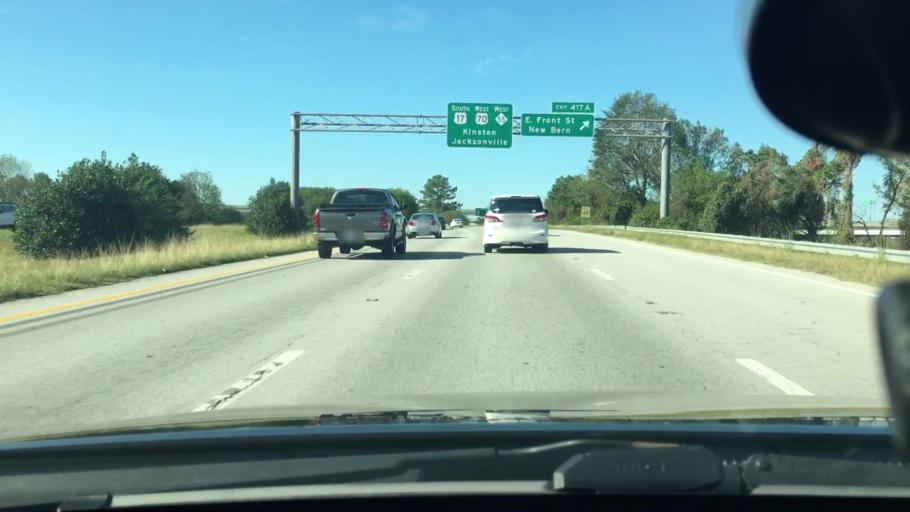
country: US
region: North Carolina
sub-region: Craven County
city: James City
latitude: 35.0910
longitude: -77.0364
